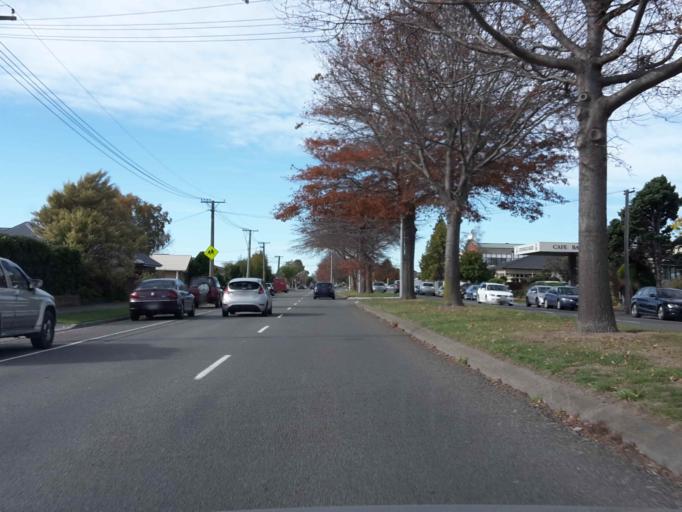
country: NZ
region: Canterbury
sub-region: Christchurch City
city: Christchurch
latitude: -43.4837
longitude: 172.5778
